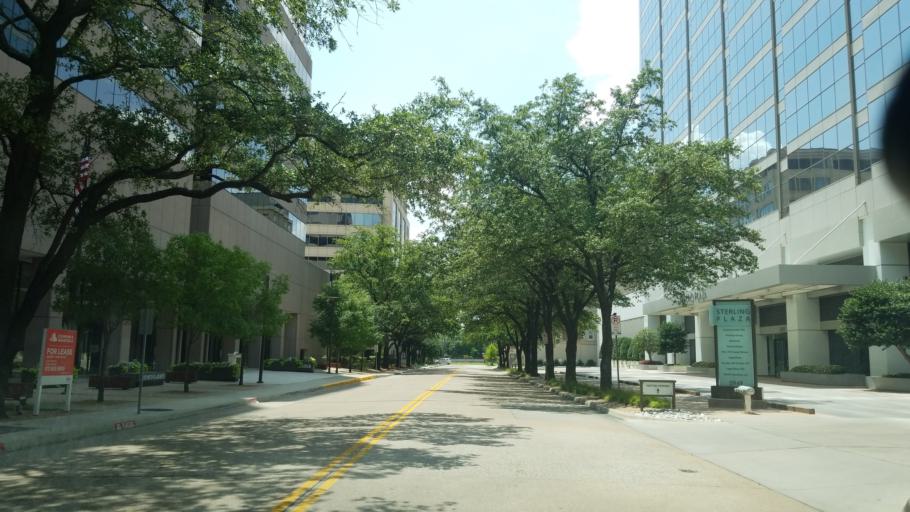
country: US
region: Texas
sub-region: Dallas County
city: University Park
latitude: 32.8624
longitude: -96.8093
